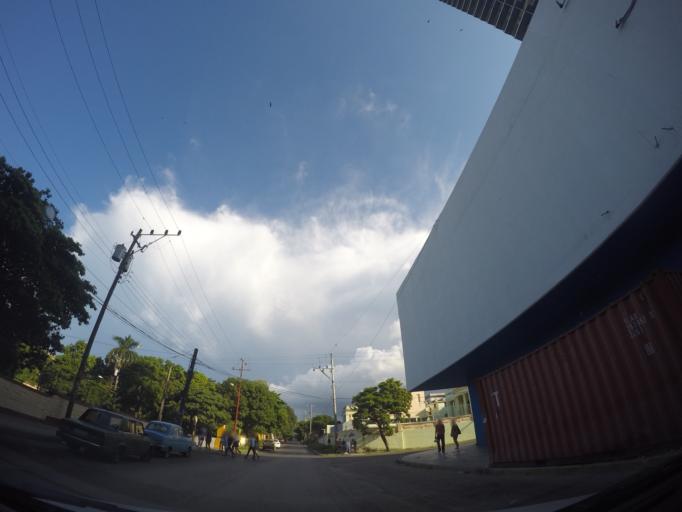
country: CU
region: La Habana
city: Havana
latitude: 23.1394
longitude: -82.3818
